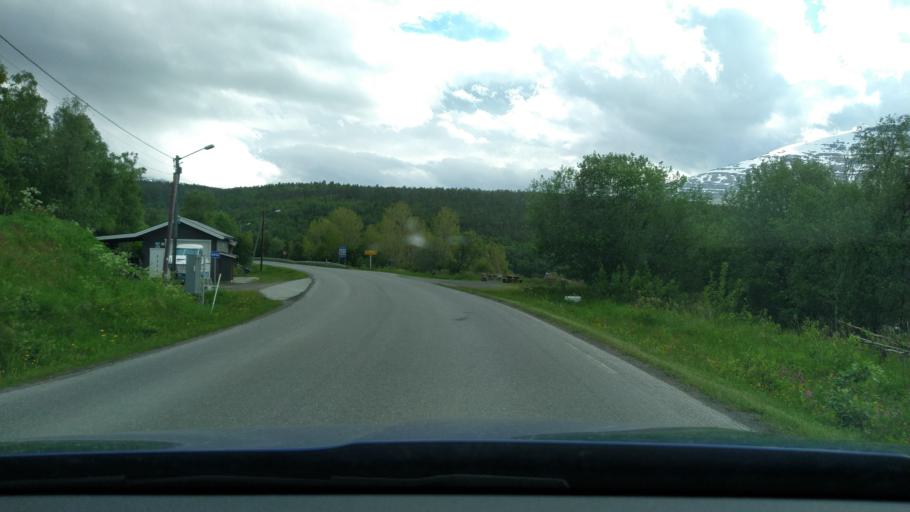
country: NO
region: Troms
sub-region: Salangen
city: Sjovegan
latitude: 68.8694
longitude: 17.8529
